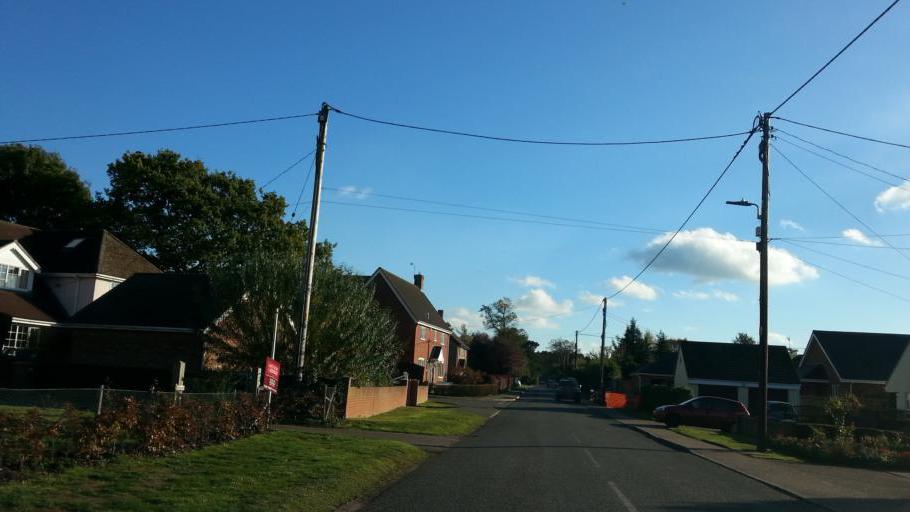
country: GB
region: England
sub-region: Suffolk
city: Thurston
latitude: 52.2540
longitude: 0.8052
